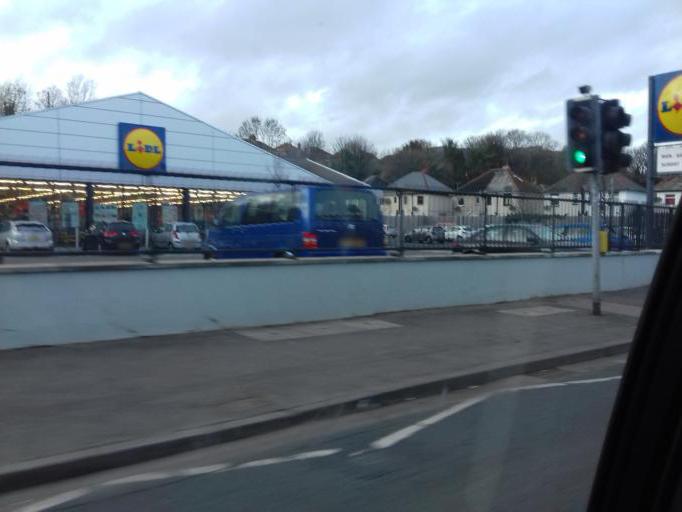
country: GB
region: Northern Ireland
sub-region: Newtownabbey District
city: Newtownabbey
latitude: 54.6267
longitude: -5.9238
